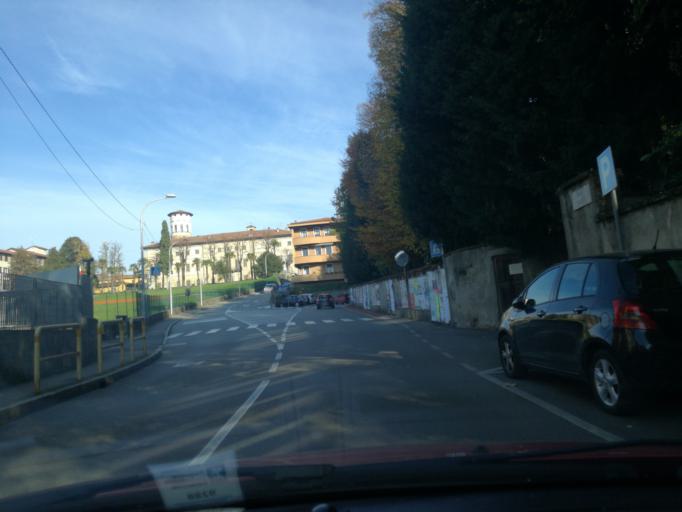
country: IT
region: Lombardy
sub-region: Provincia di Lecco
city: Merate
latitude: 45.6959
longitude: 9.4166
